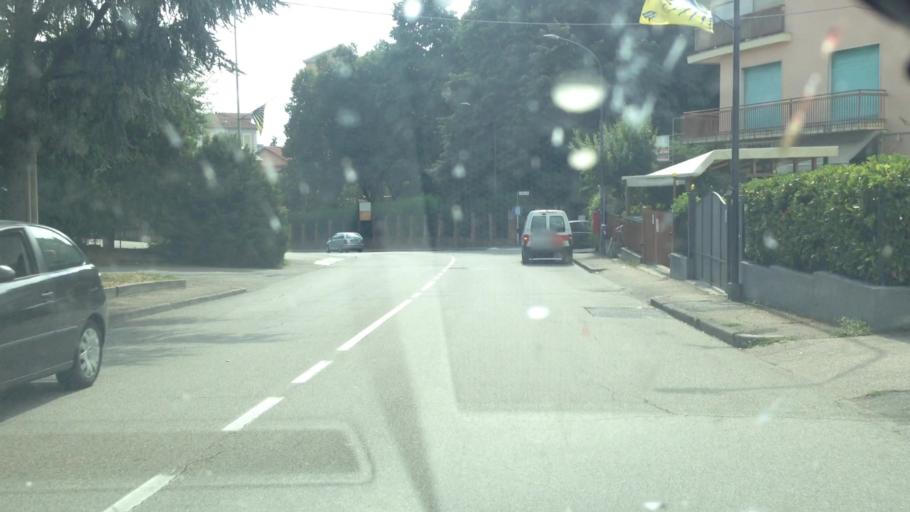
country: IT
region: Piedmont
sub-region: Provincia di Asti
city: Asti
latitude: 44.9077
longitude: 8.2072
